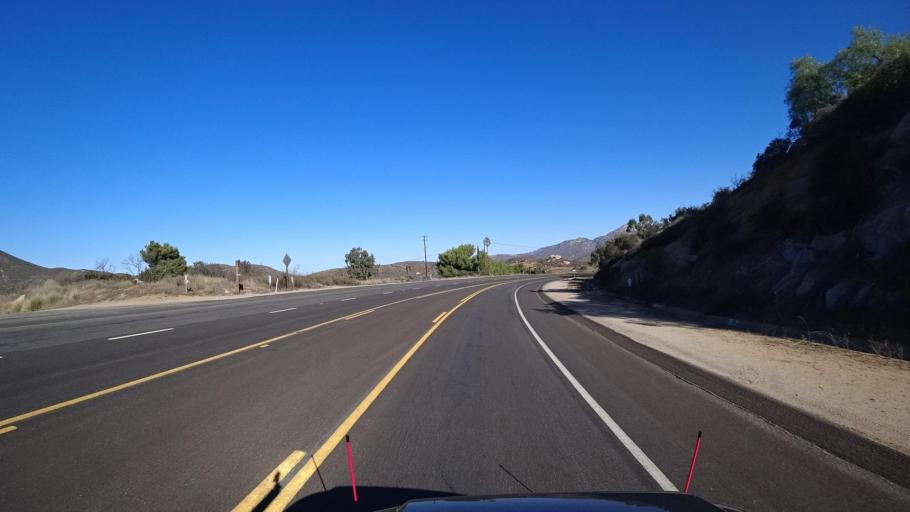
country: MX
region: Baja California
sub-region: Tijuana
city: Villa del Campo
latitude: 32.6223
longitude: -116.7650
